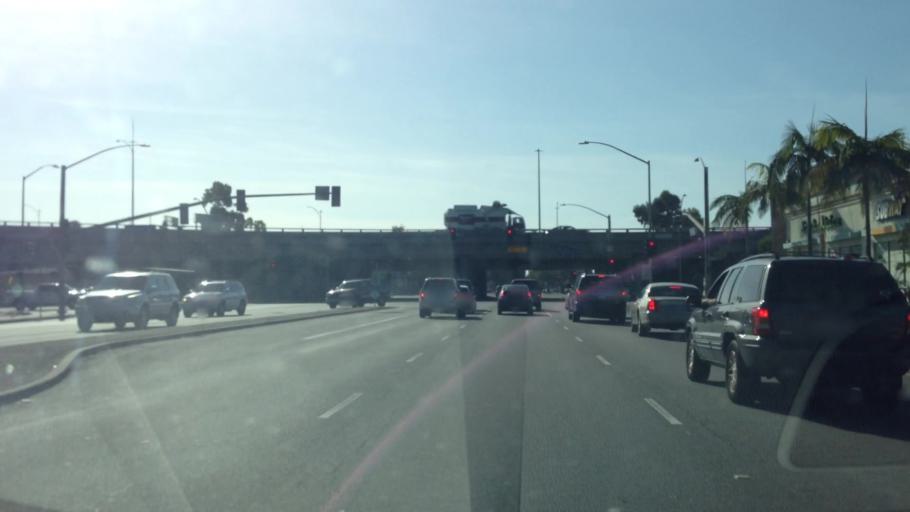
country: US
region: California
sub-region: Los Angeles County
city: Signal Hill
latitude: 33.8040
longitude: -118.1252
